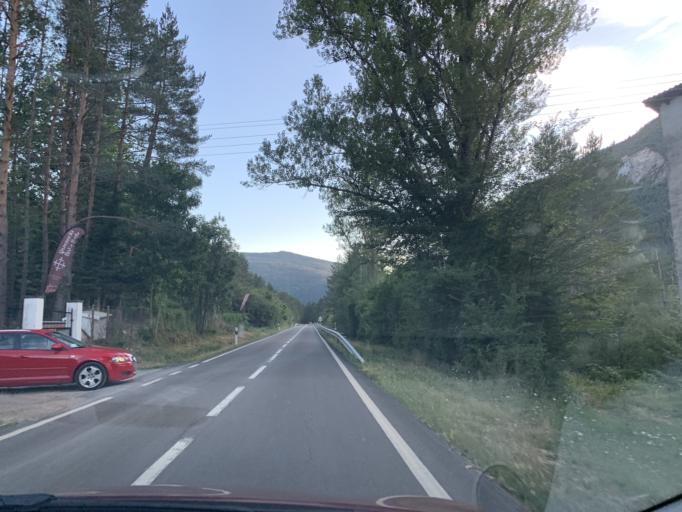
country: ES
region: Aragon
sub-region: Provincia de Huesca
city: Broto
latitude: 42.5585
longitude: -0.1186
